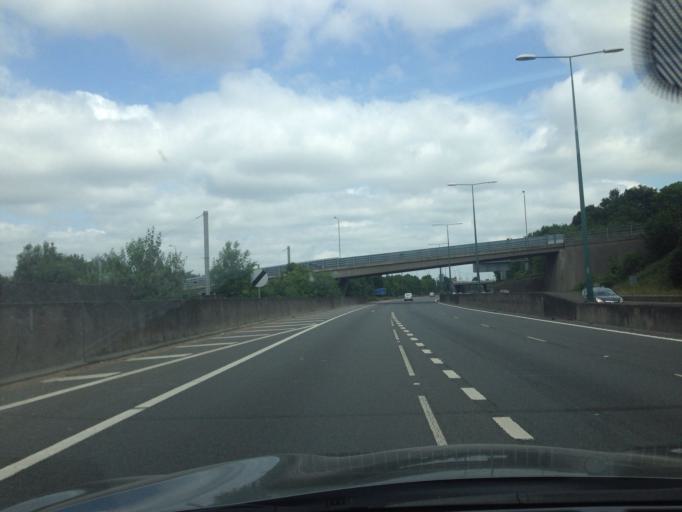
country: GB
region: England
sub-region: Greater London
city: Hendon
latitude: 51.5760
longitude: -0.2357
